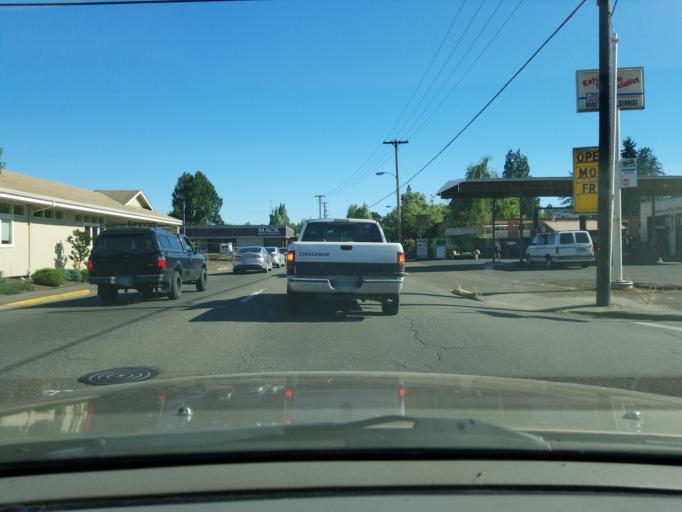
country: US
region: Oregon
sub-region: Yamhill County
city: McMinnville
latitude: 45.2129
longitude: -123.1990
